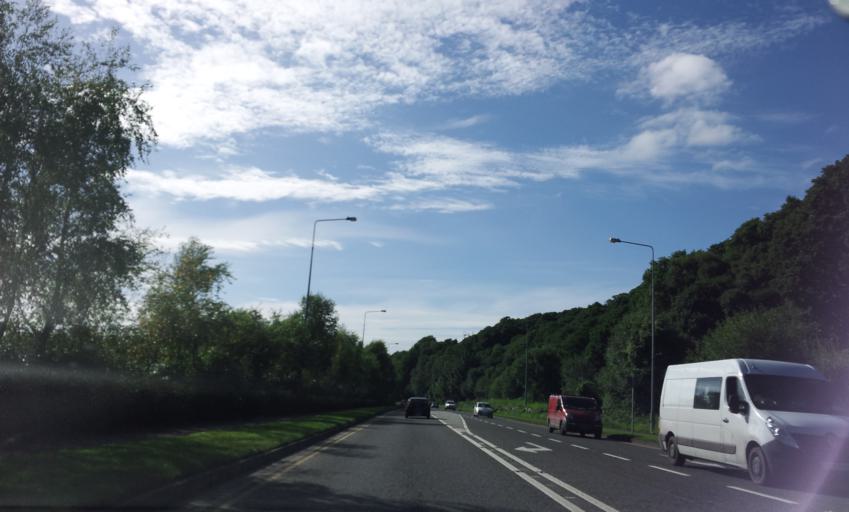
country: IE
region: Munster
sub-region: Ciarrai
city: Cill Airne
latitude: 52.0578
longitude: -9.4717
